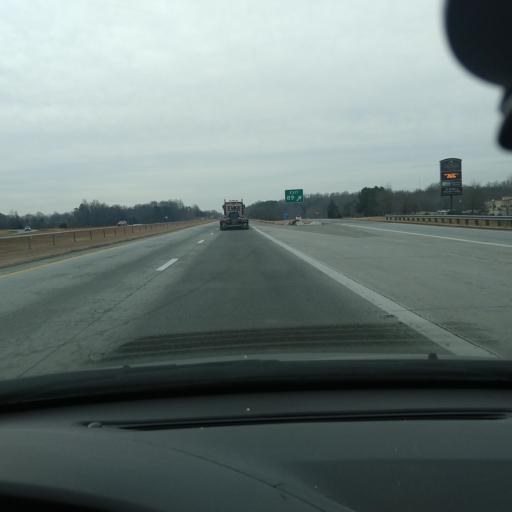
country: US
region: North Carolina
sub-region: Davidson County
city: Lexington
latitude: 35.8406
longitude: -80.2823
